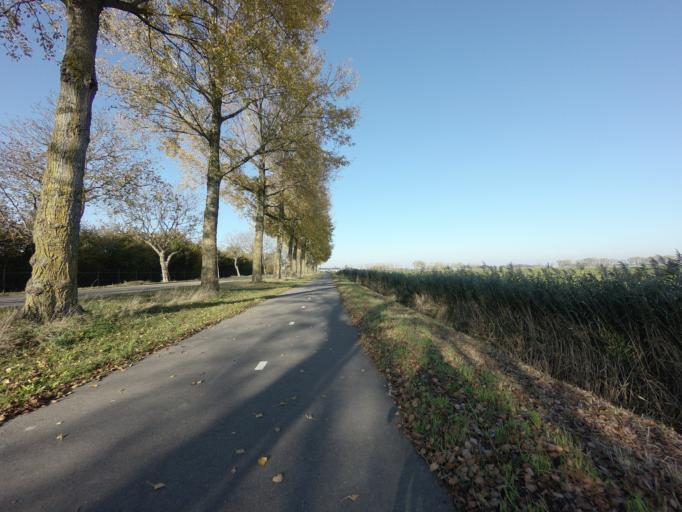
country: NL
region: North Brabant
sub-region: Gemeente Waalwijk
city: Waalwijk
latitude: 51.7235
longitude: 5.0566
